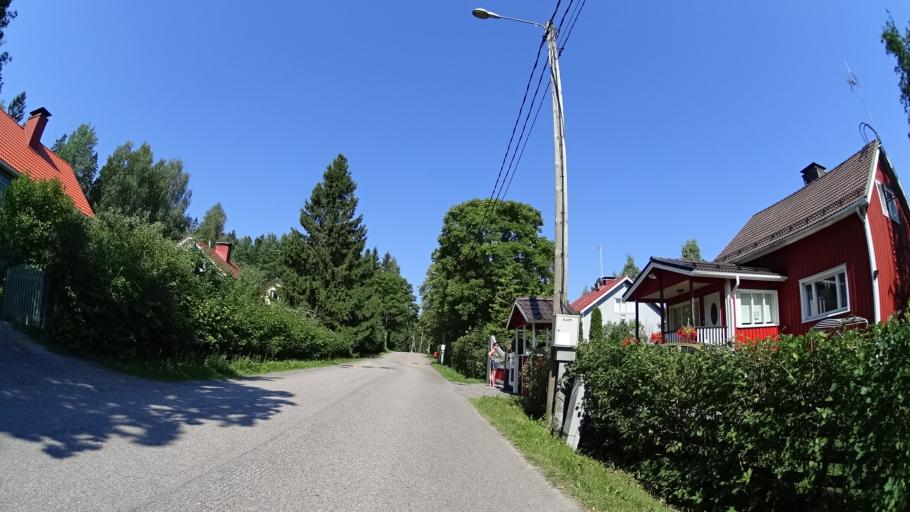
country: FI
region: Uusimaa
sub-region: Helsinki
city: Kerava
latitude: 60.3743
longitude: 25.0836
